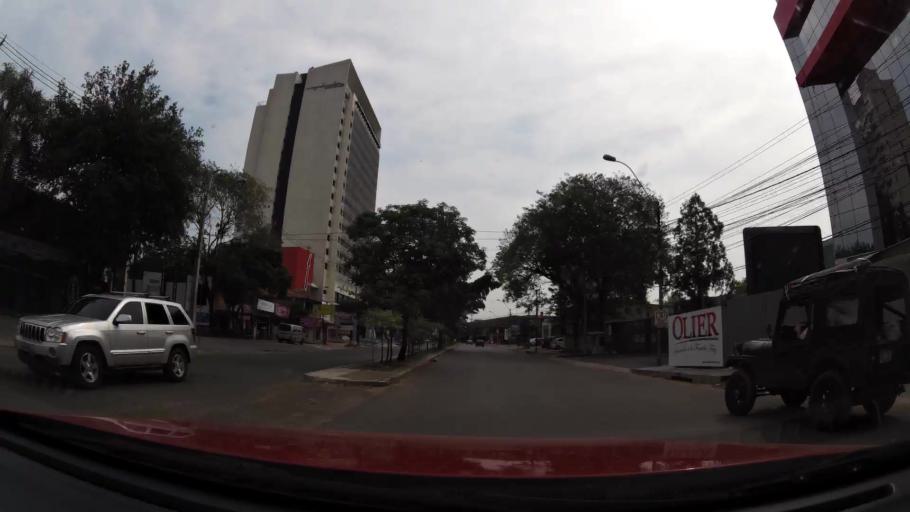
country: PY
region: Central
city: Fernando de la Mora
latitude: -25.2802
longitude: -57.5589
